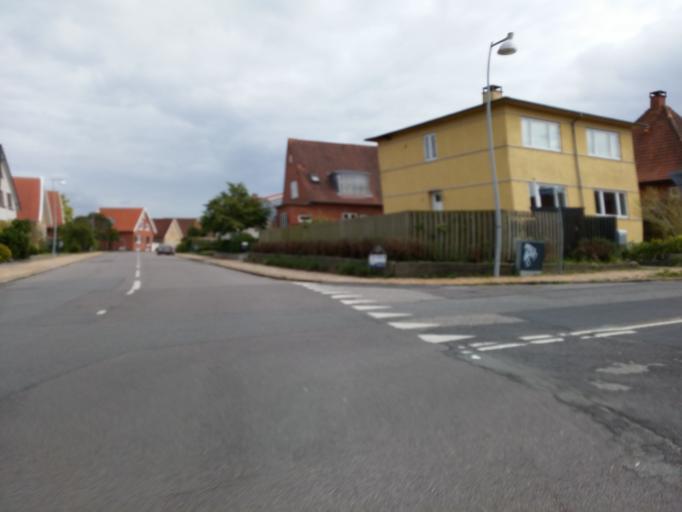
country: DK
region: South Denmark
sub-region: Odense Kommune
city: Odense
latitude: 55.4102
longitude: 10.4024
